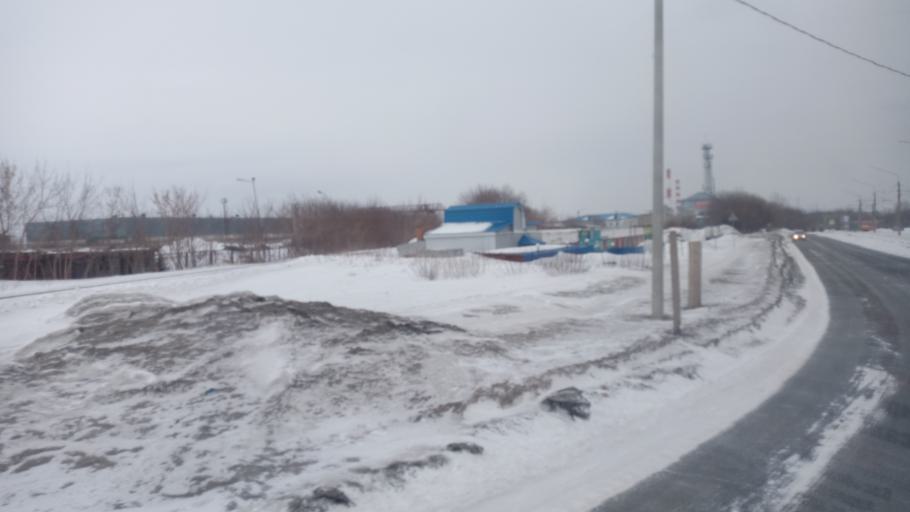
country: RU
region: Altai Krai
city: Novosilikatnyy
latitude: 53.3900
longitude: 83.6727
